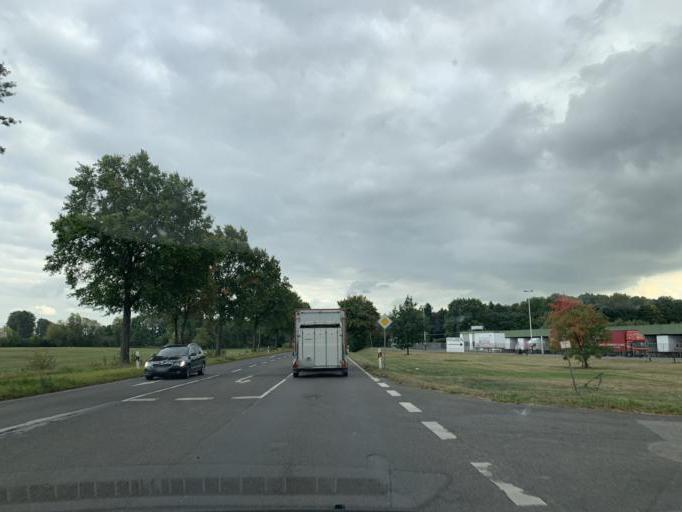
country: DE
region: North Rhine-Westphalia
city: Huckelhoven
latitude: 51.0314
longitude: 6.2190
